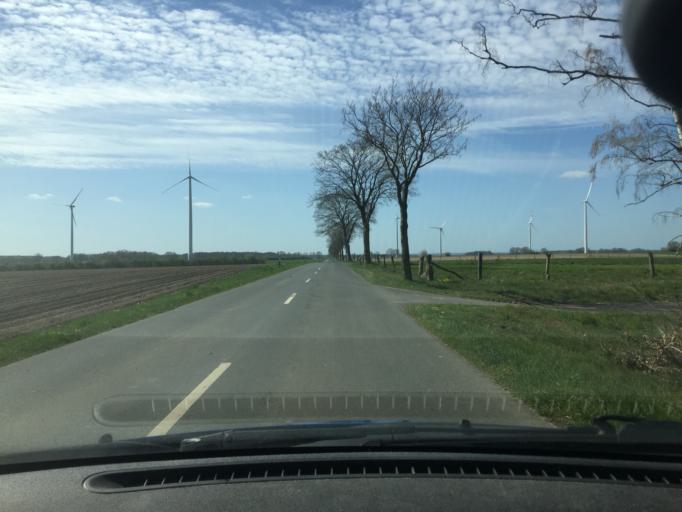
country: DE
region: Lower Saxony
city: Ratzlingen
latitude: 52.9530
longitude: 10.6677
